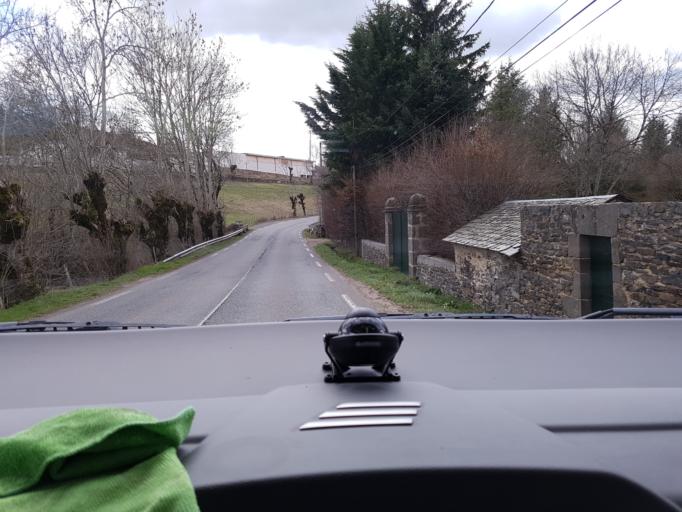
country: FR
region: Midi-Pyrenees
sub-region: Departement de l'Aveyron
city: Laguiole
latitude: 44.6882
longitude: 2.8541
